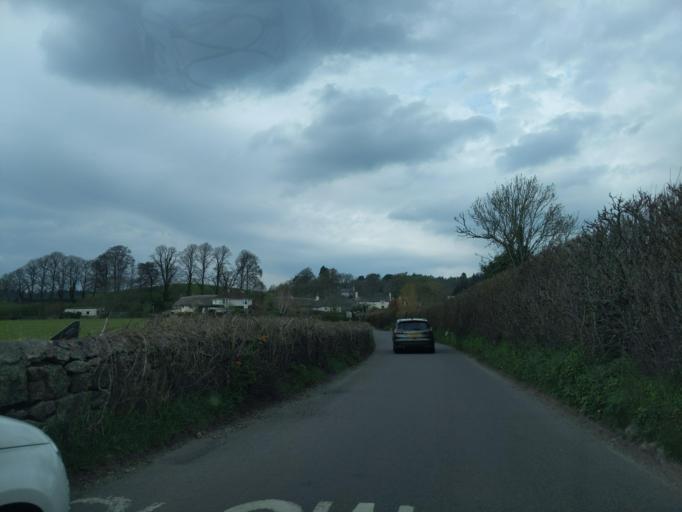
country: GB
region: England
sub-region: Devon
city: Bovey Tracey
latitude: 50.6901
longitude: -3.8236
